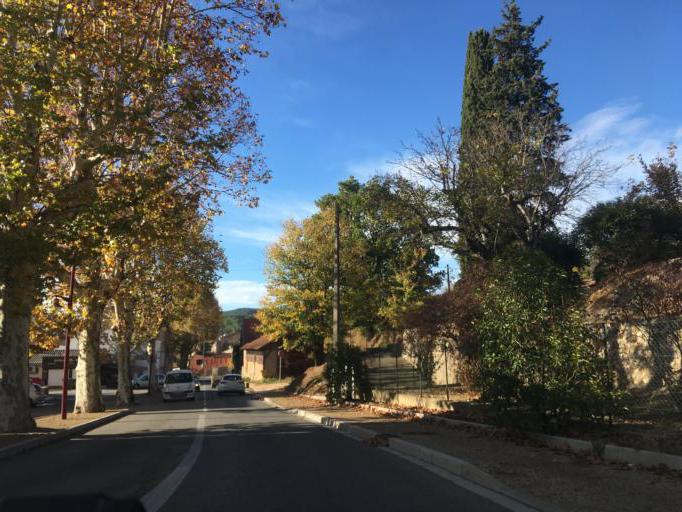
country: FR
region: Provence-Alpes-Cote d'Azur
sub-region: Departement du Var
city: Salernes
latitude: 43.5615
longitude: 6.2381
